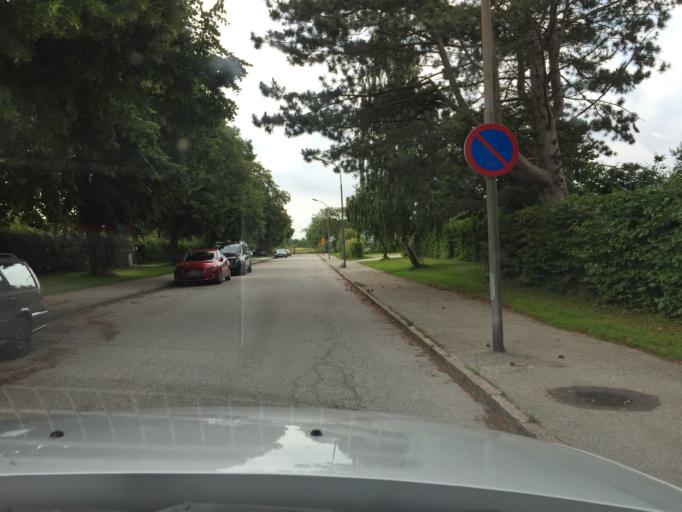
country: SE
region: Skane
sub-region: Lunds Kommun
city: Lund
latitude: 55.7002
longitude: 13.1653
